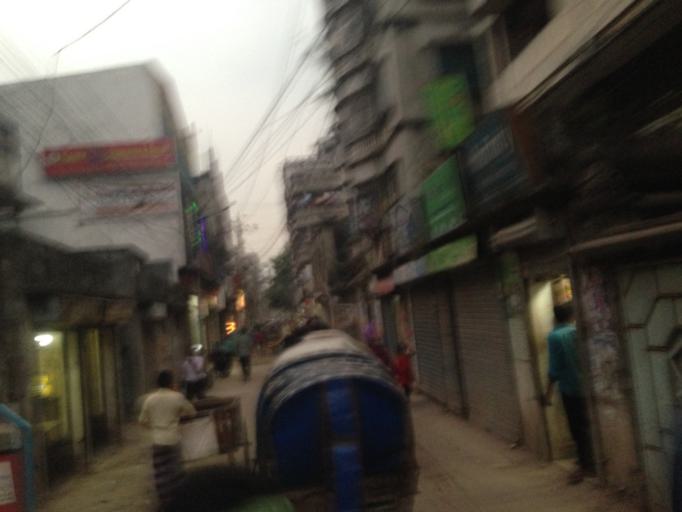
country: BD
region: Dhaka
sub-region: Dhaka
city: Dhaka
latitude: 23.7046
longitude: 90.4239
